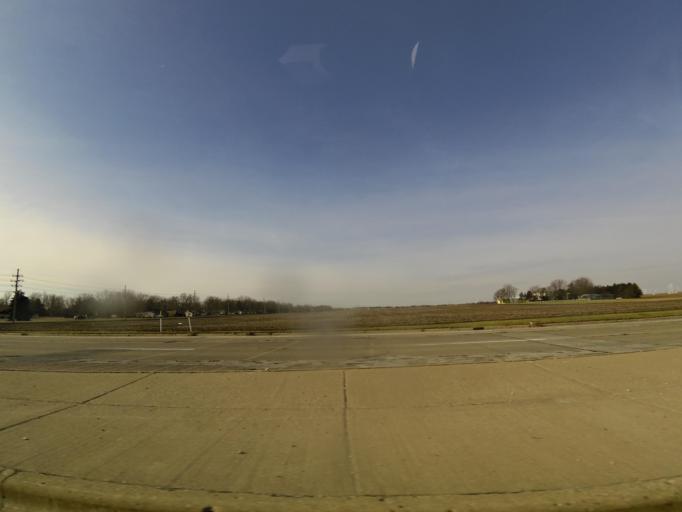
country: US
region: Illinois
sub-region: Macon County
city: Forsyth
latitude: 39.9359
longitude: -88.9556
